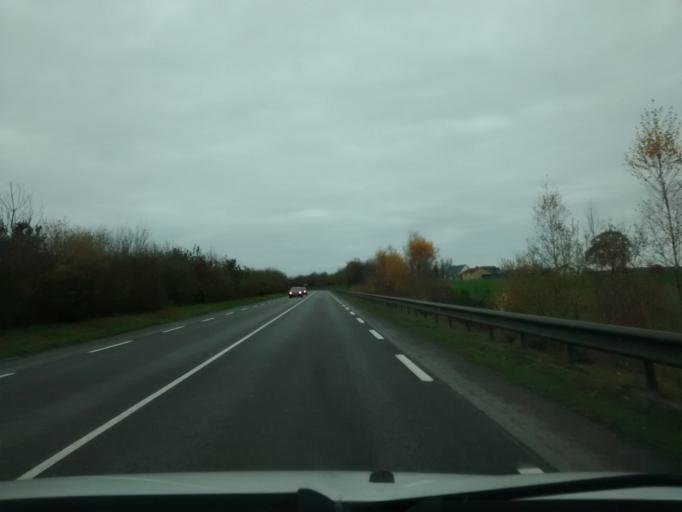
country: FR
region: Brittany
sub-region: Departement d'Ille-et-Vilaine
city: Etrelles
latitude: 48.0654
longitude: -1.1865
